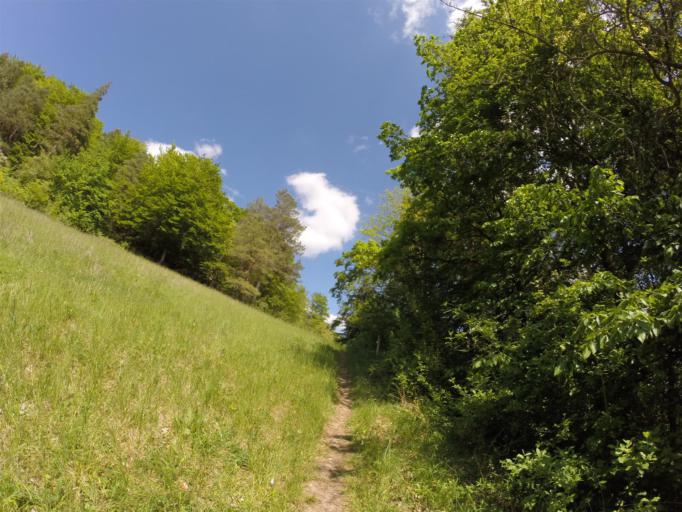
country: DE
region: Thuringia
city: Loberschutz
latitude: 50.9734
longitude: 11.7003
